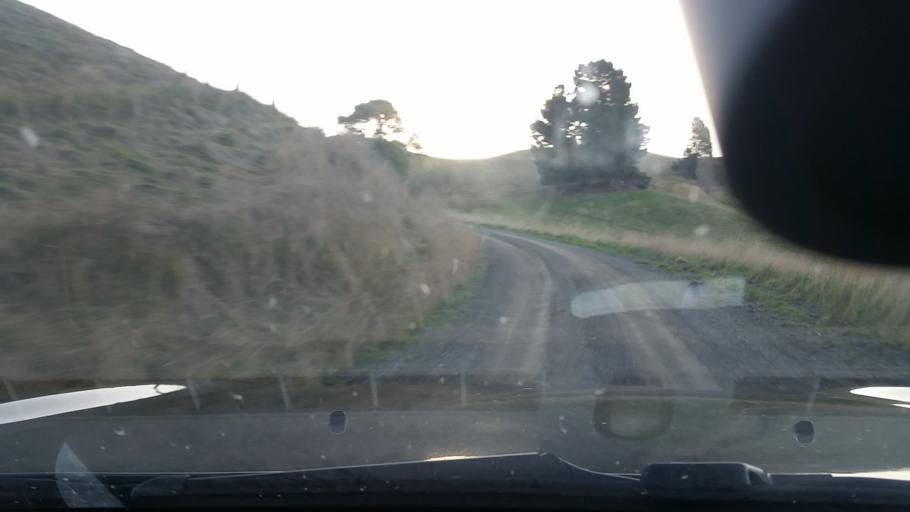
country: NZ
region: Marlborough
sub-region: Marlborough District
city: Blenheim
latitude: -41.7424
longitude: 174.0505
